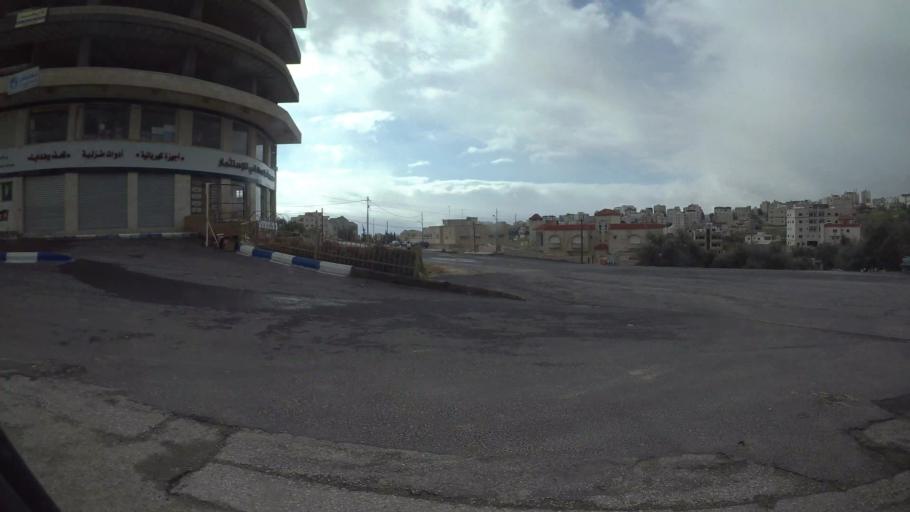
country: JO
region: Amman
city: Al Jubayhah
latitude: 32.0552
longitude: 35.8905
